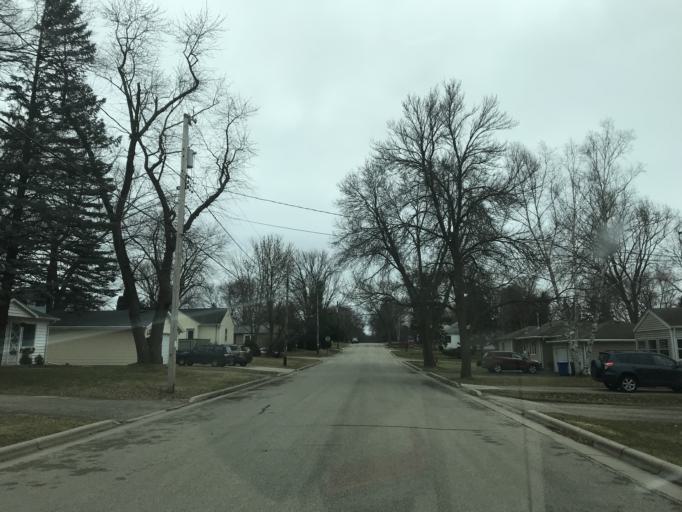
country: US
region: Wisconsin
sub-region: Dane County
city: Monona
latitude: 43.0689
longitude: -89.3283
